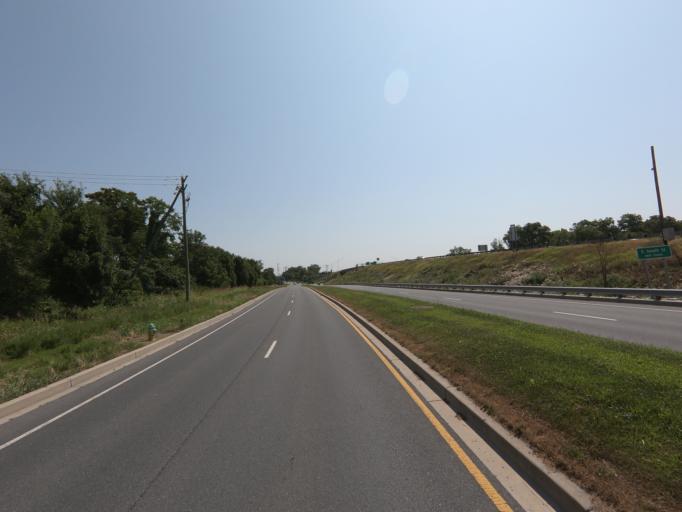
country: US
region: Maryland
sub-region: Frederick County
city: Frederick
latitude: 39.4038
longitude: -77.3967
